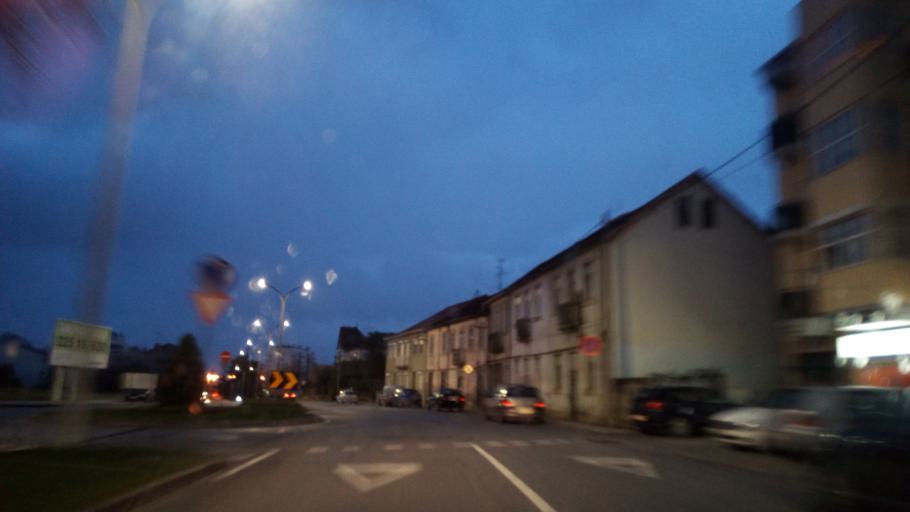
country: PT
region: Viseu
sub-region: Viseu
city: Viseu
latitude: 40.6517
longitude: -7.9132
